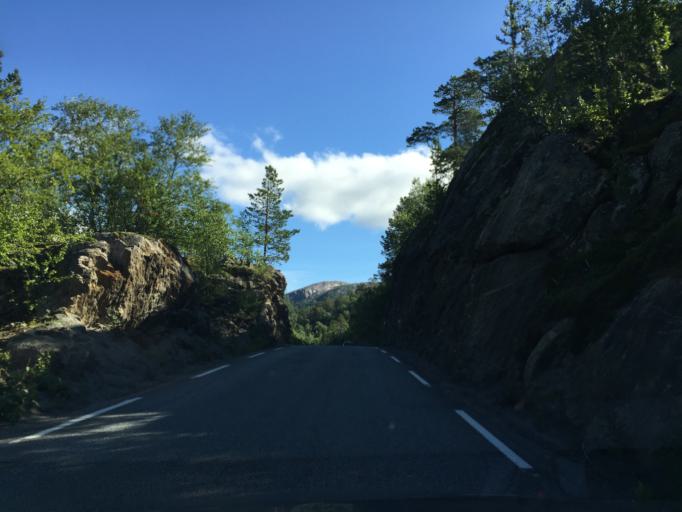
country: NO
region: Nordland
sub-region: Saltdal
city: Rognan
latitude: 66.8153
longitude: 15.4450
